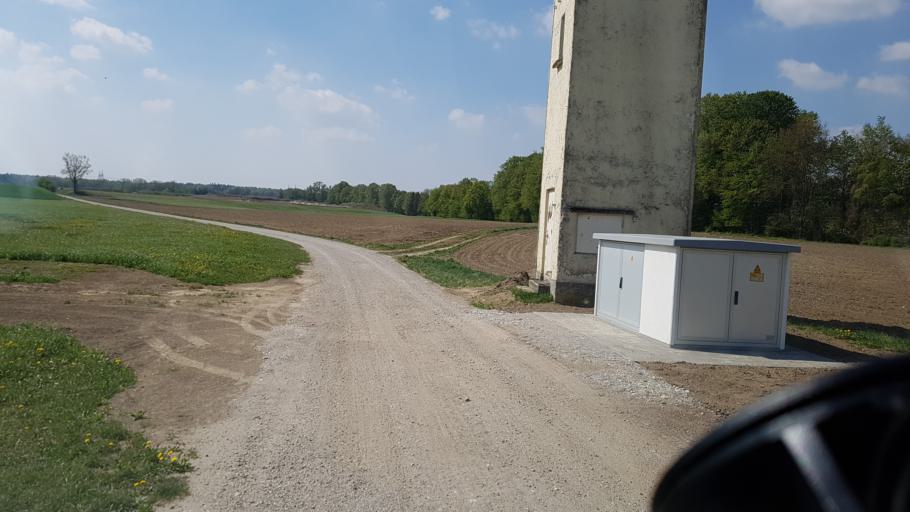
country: DE
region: Bavaria
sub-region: Upper Bavaria
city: Perach
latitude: 48.2596
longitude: 12.8030
